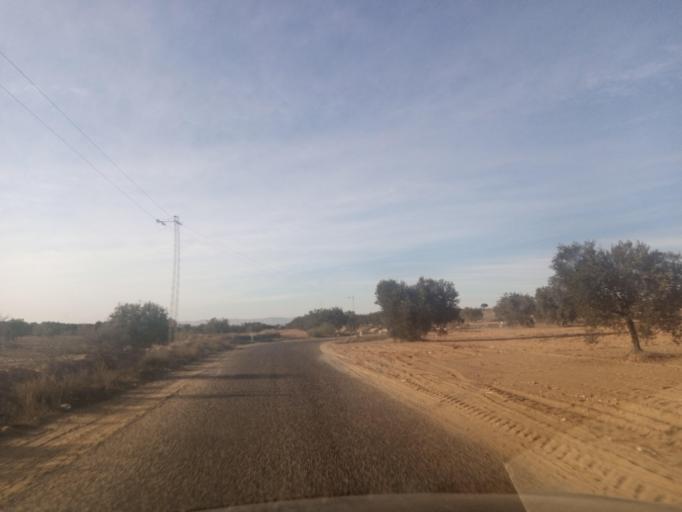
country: TN
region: Safaqis
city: Bi'r `Ali Bin Khalifah
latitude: 34.8448
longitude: 10.1600
